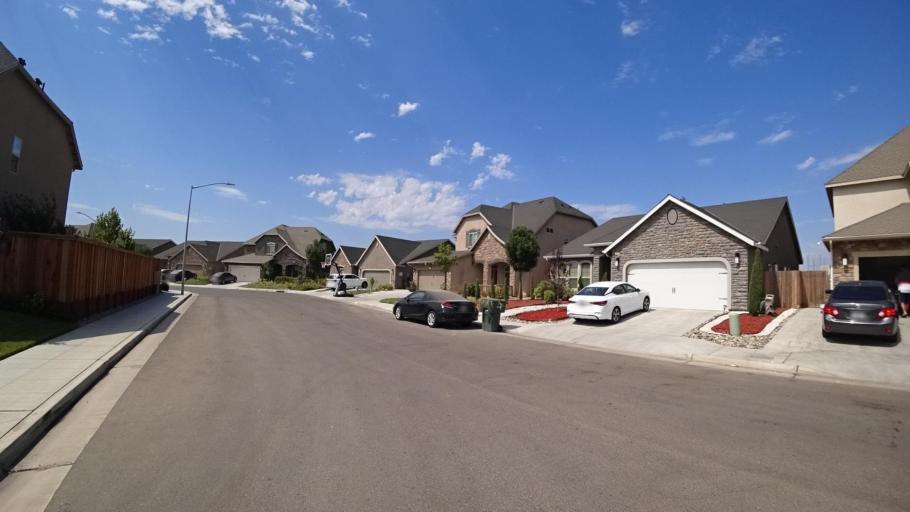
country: US
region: California
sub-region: Fresno County
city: Tarpey Village
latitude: 36.7853
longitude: -119.6689
